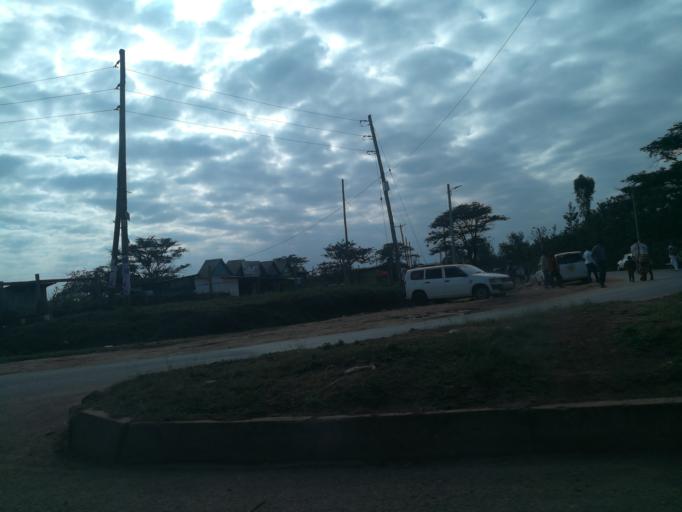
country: KE
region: Nairobi Area
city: Thika
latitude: -1.1247
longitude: 37.0030
